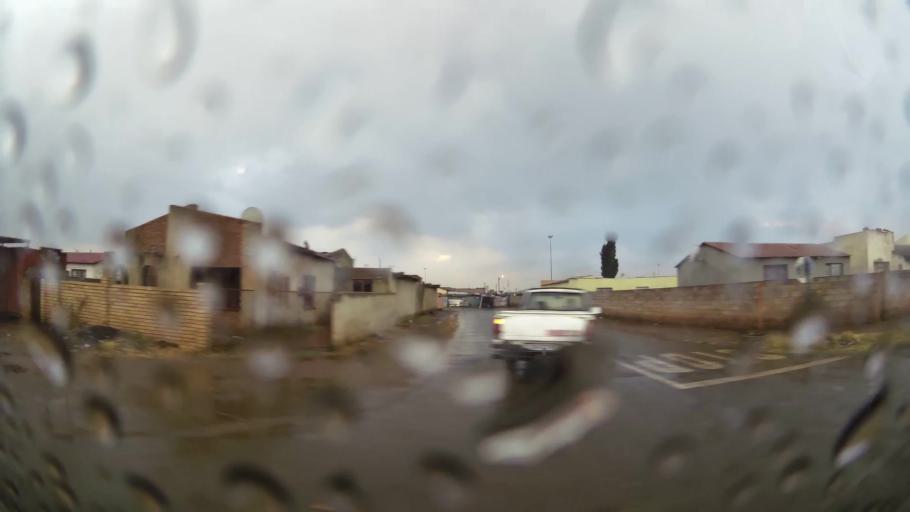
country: ZA
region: Gauteng
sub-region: Ekurhuleni Metropolitan Municipality
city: Germiston
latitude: -26.3493
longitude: 28.1405
